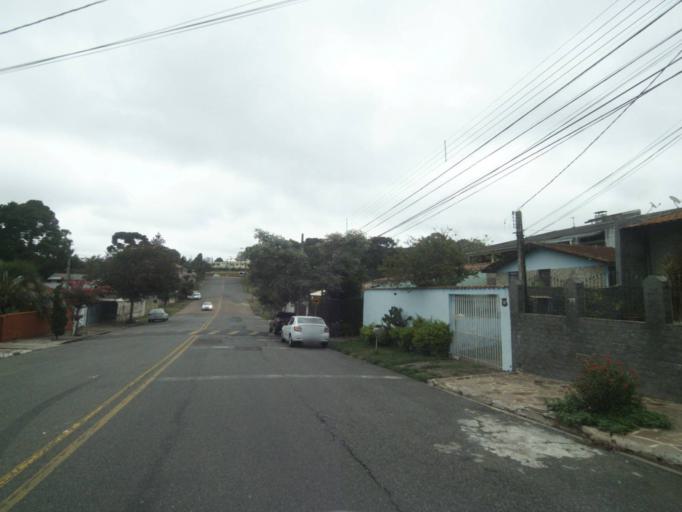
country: BR
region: Parana
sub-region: Curitiba
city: Curitiba
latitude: -25.4287
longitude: -49.3407
